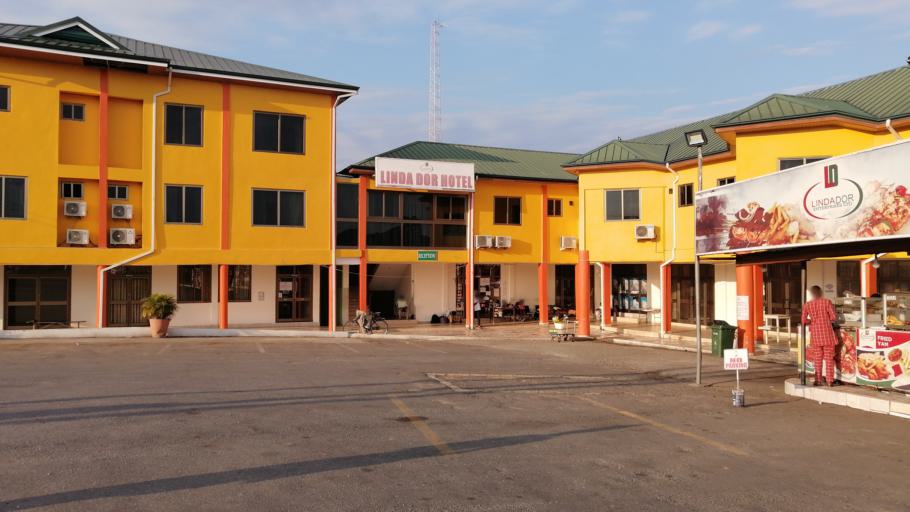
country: GH
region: Eastern
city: Begoro
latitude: 6.2908
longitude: -0.4748
